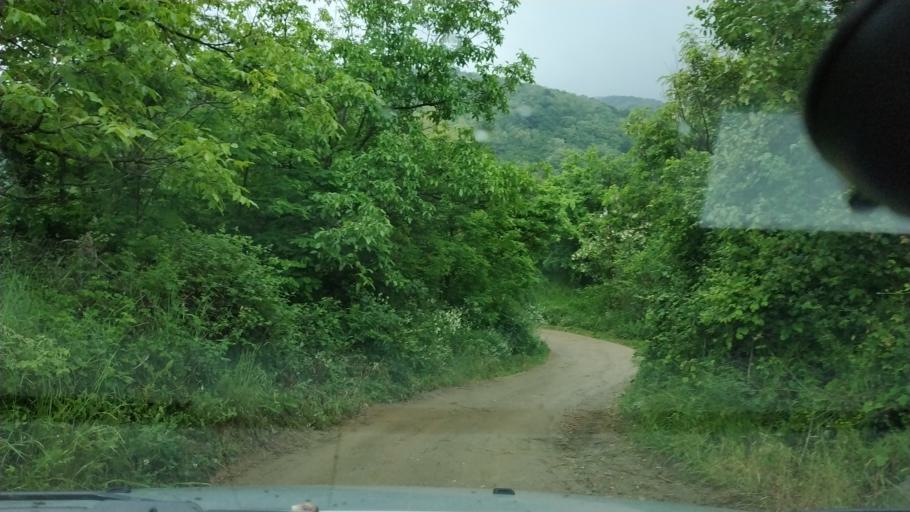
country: RS
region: Central Serbia
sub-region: Toplicki Okrug
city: Prokuplje
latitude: 43.4001
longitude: 21.5530
